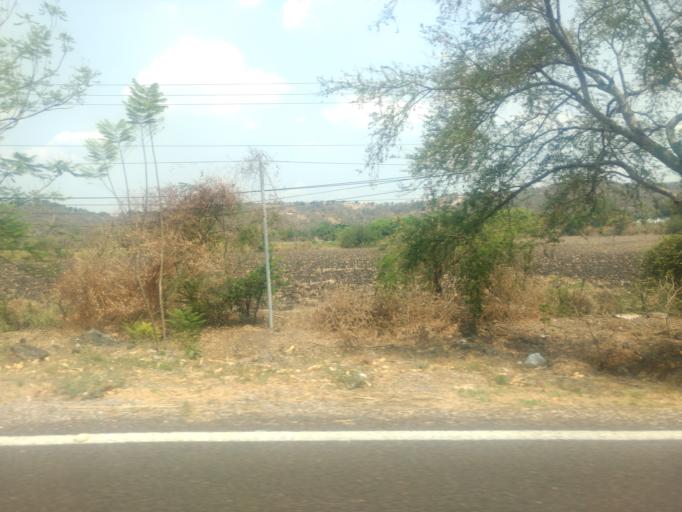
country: MX
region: Morelos
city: Puente de Ixtla
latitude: 18.6372
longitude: -99.3134
